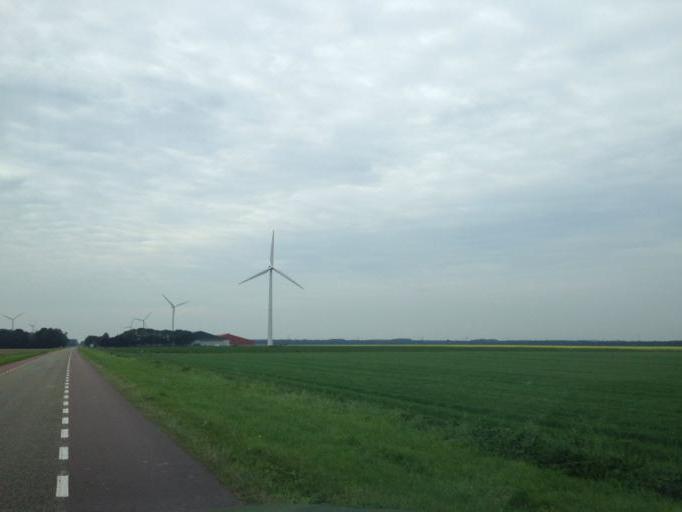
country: NL
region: Flevoland
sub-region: Gemeente Lelystad
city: Lelystad
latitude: 52.4023
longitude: 5.4244
